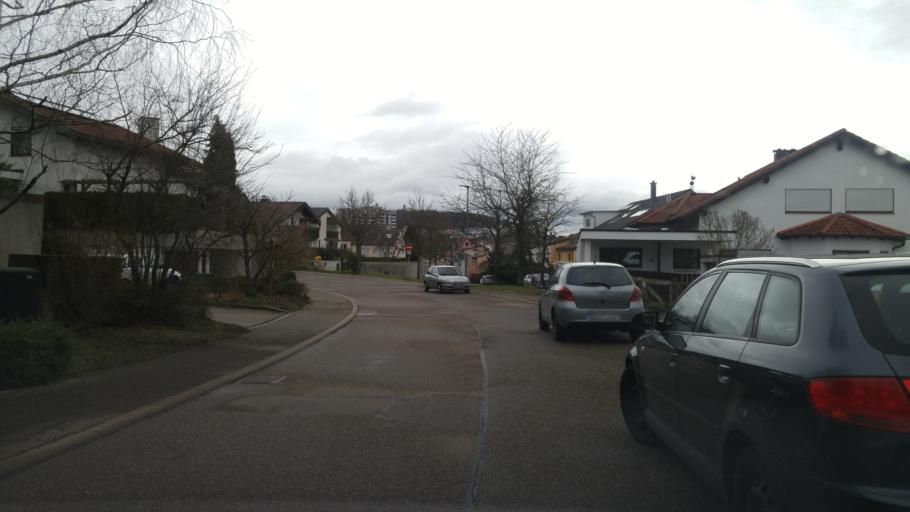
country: DE
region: Baden-Wuerttemberg
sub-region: Regierungsbezirk Stuttgart
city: Leonberg
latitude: 48.8081
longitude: 9.0072
